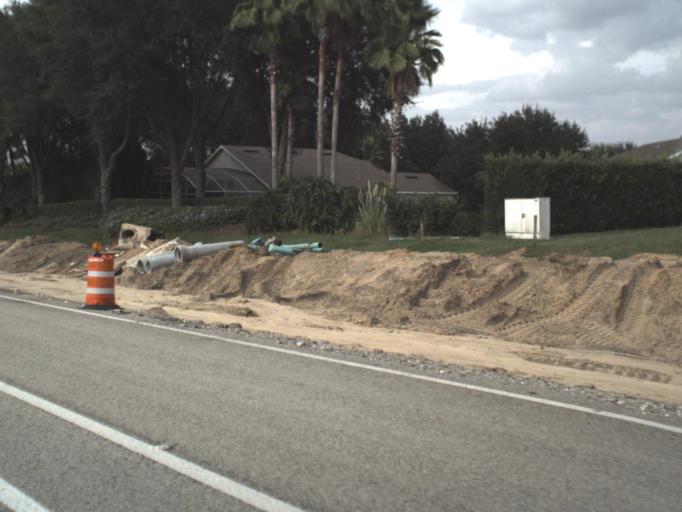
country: US
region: Florida
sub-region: Lake County
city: Four Corners
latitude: 28.2911
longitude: -81.6644
